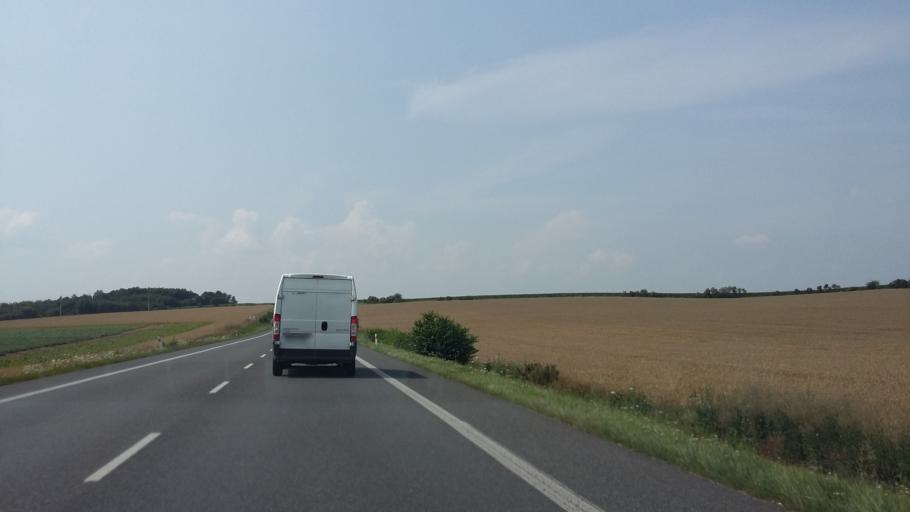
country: CZ
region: Central Bohemia
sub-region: Okres Melnik
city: Veltrusy
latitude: 50.3198
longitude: 14.3342
